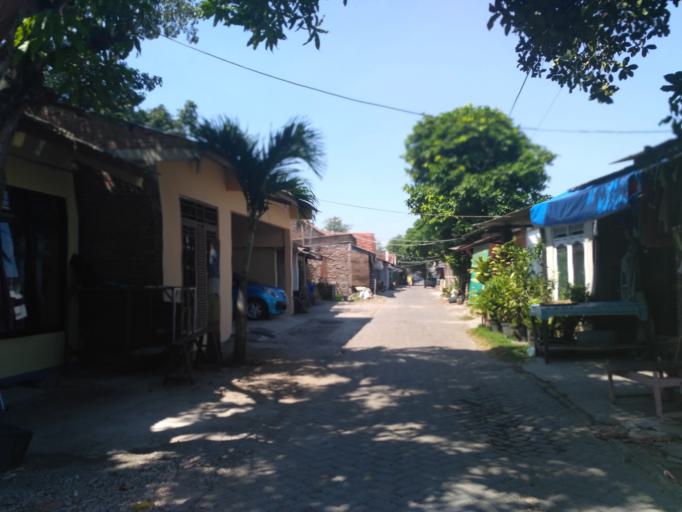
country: ID
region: Central Java
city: Semarang
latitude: -7.0029
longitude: 110.4458
